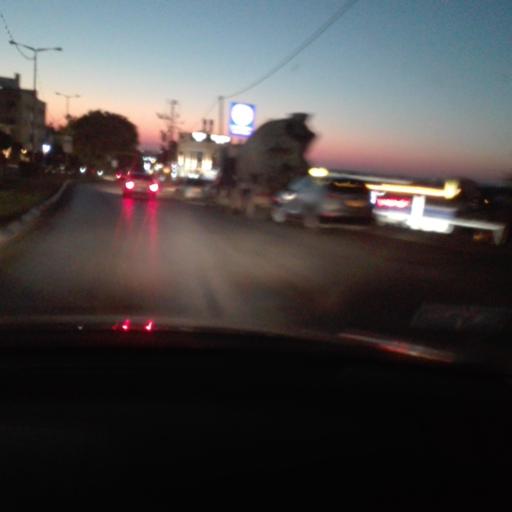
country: PS
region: West Bank
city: Nazlat `Isa
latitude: 32.4242
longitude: 35.0370
